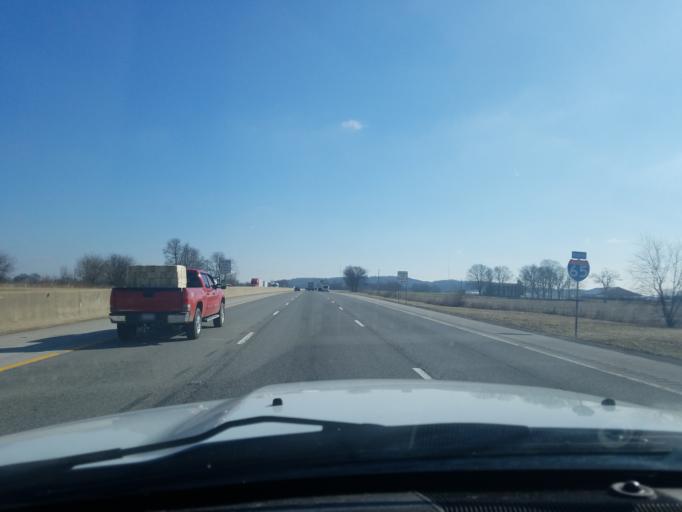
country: US
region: Kentucky
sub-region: Edmonson County
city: Brownsville
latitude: 37.0413
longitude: -86.2027
